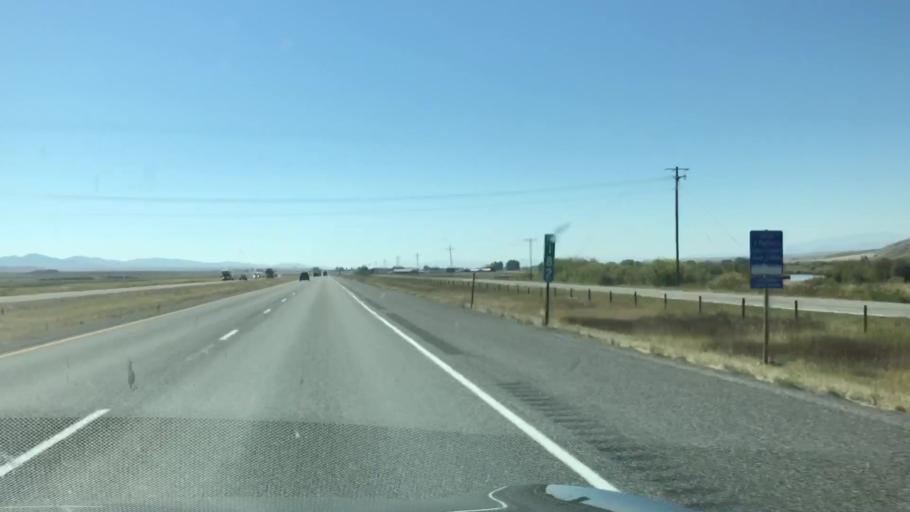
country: US
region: Montana
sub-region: Powell County
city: Deer Lodge
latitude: 46.4490
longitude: -112.7226
